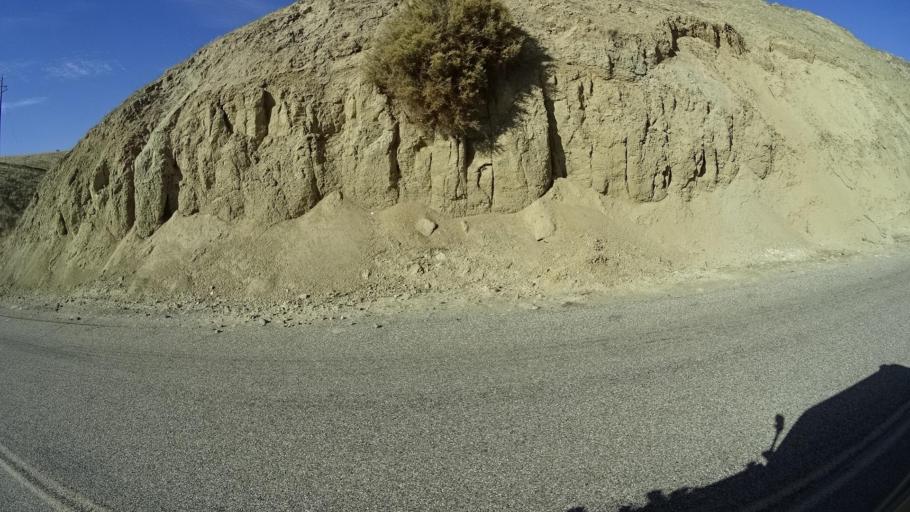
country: US
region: California
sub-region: Kern County
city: Oildale
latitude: 35.5265
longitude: -118.9409
